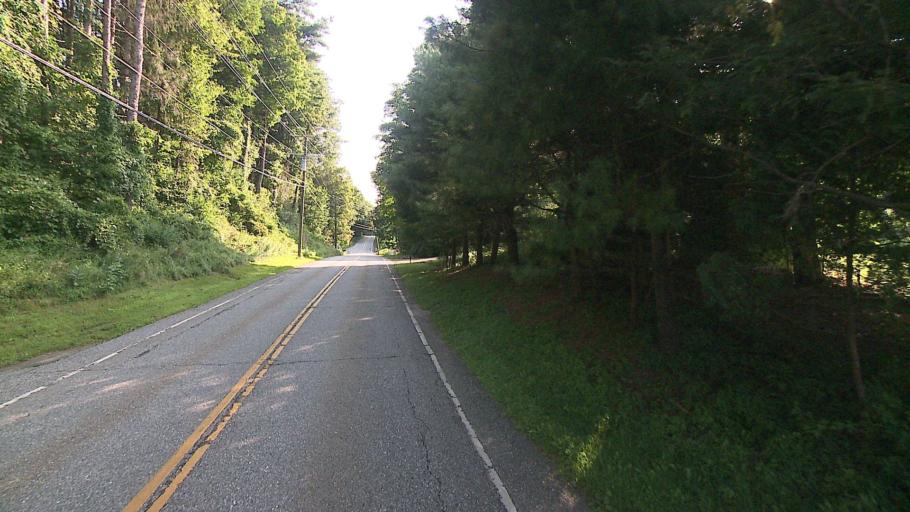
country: US
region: Connecticut
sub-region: Litchfield County
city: Kent
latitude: 41.8020
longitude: -73.3873
